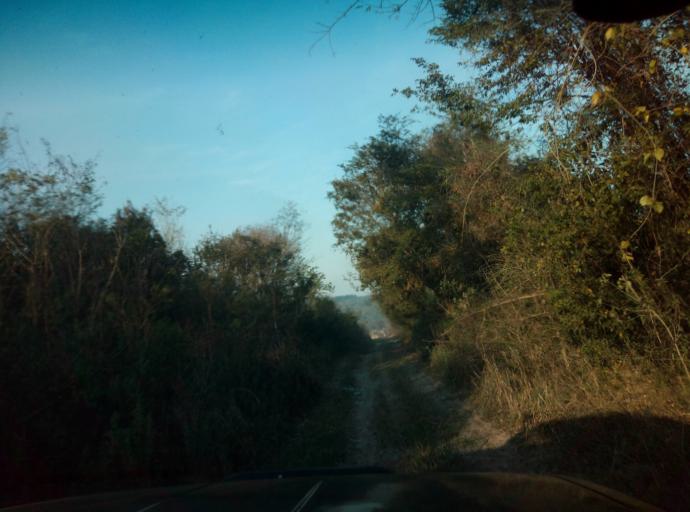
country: PY
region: Caaguazu
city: Doctor Cecilio Baez
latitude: -25.1997
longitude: -56.1178
